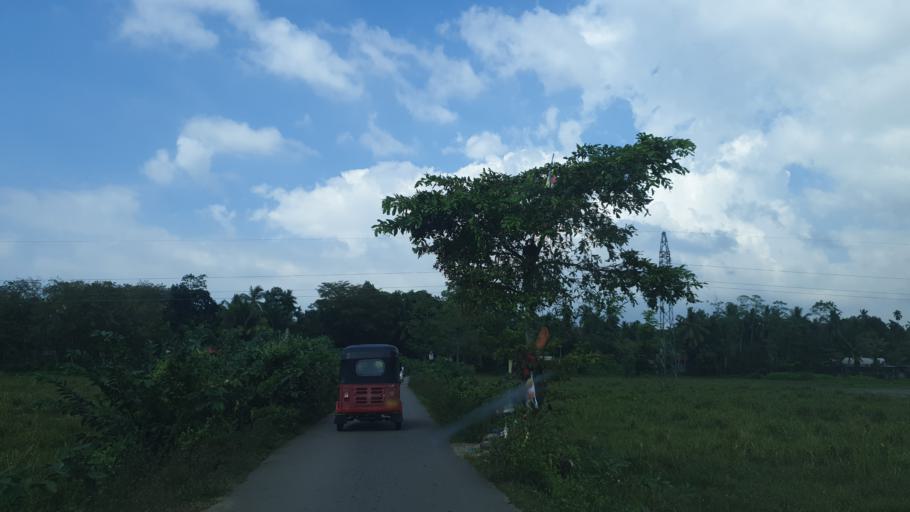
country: LK
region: Western
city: Horana South
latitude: 6.7025
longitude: 79.9856
